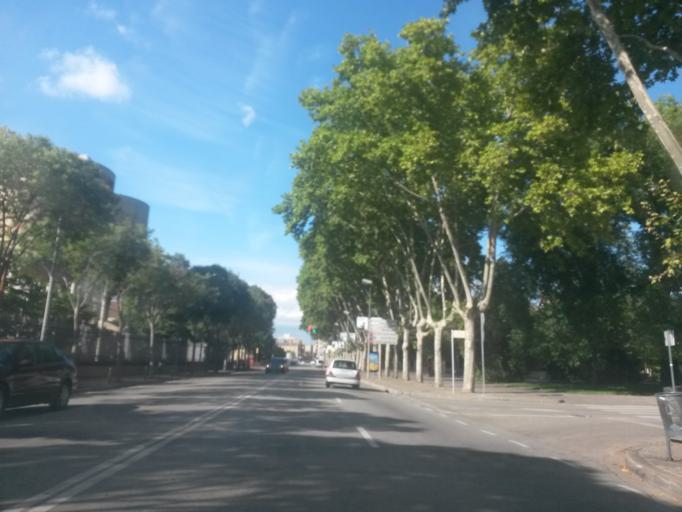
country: ES
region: Catalonia
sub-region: Provincia de Girona
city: Girona
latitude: 41.9727
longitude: 2.8155
